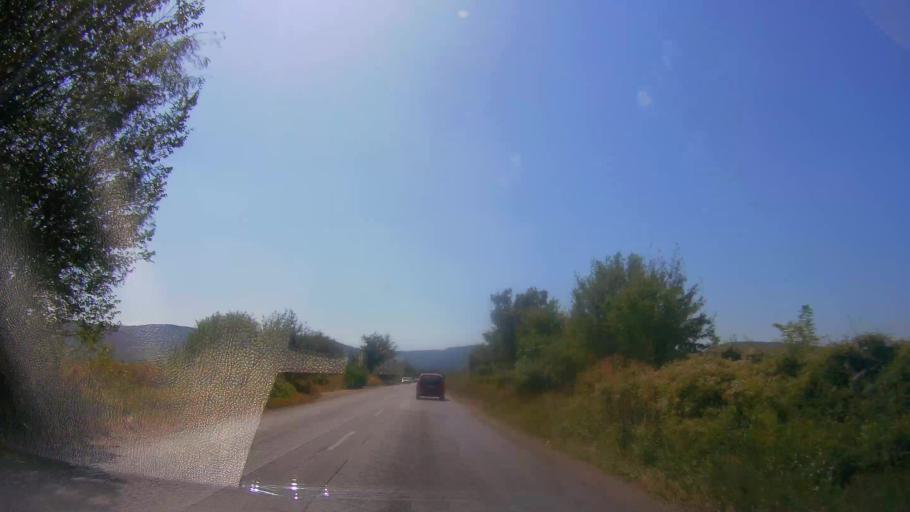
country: BG
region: Veliko Turnovo
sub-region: Obshtina Gorna Oryakhovitsa
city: Purvomaytsi
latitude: 43.1574
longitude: 25.6190
